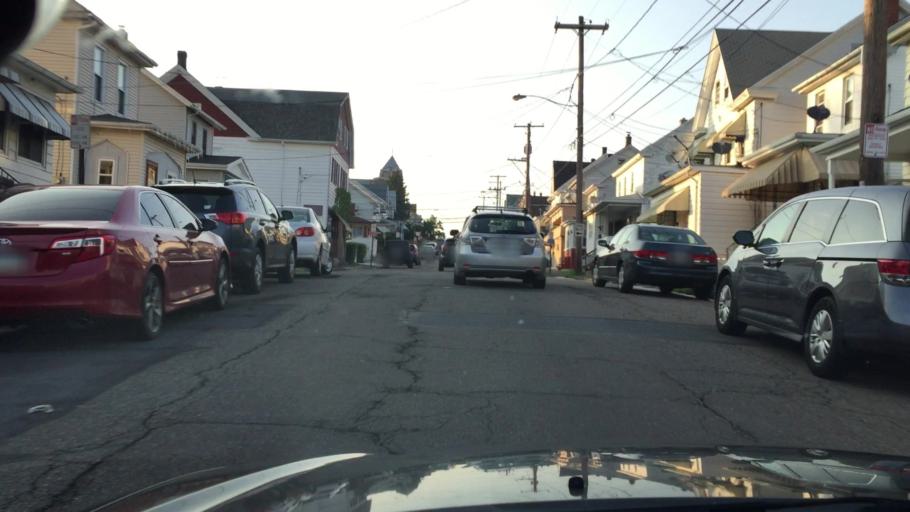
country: US
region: Pennsylvania
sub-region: Luzerne County
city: Hazleton
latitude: 40.9632
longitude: -75.9700
